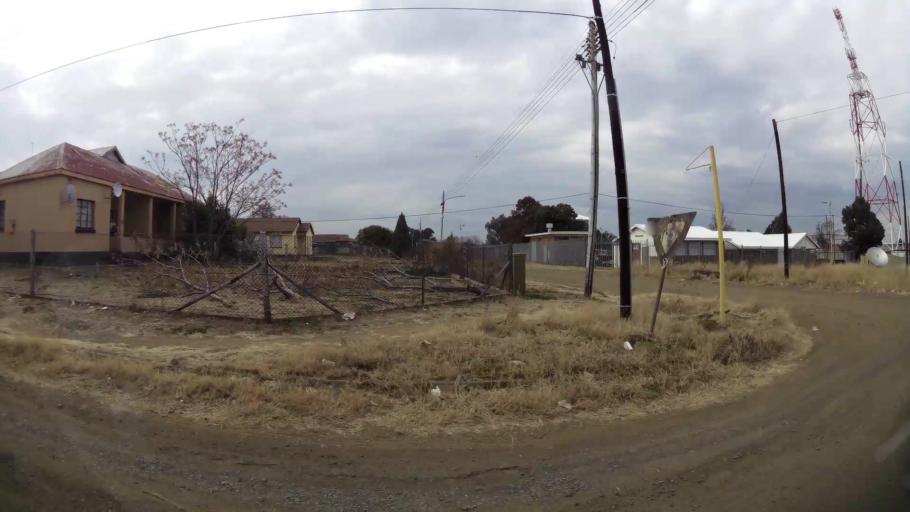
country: ZA
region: Orange Free State
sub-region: Fezile Dabi District Municipality
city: Kroonstad
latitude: -27.6579
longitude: 27.2335
